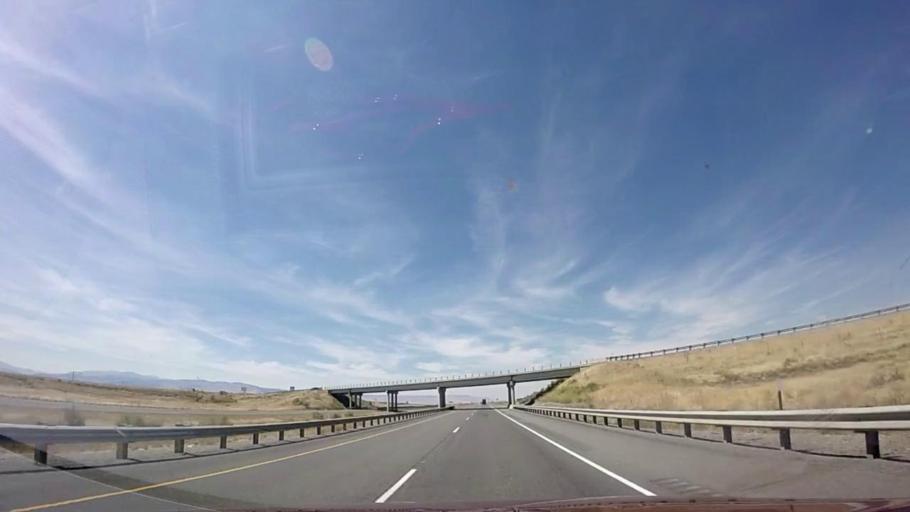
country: US
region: Idaho
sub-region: Minidoka County
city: Rupert
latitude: 42.3271
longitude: -113.2113
